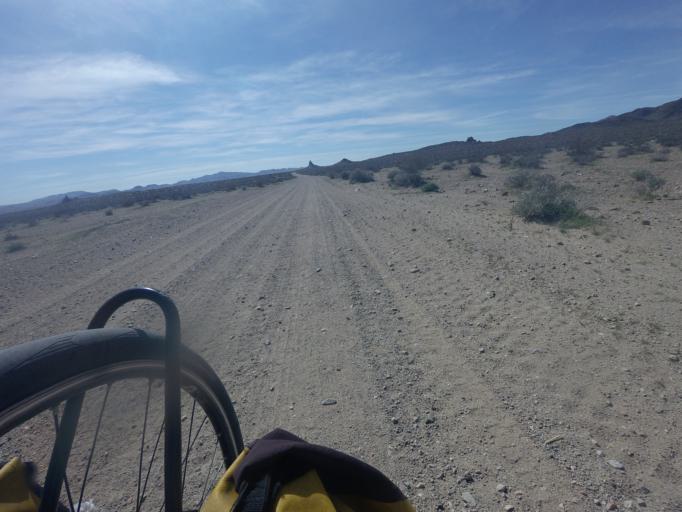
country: US
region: California
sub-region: San Bernardino County
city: Searles Valley
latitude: 35.5806
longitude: -117.4280
